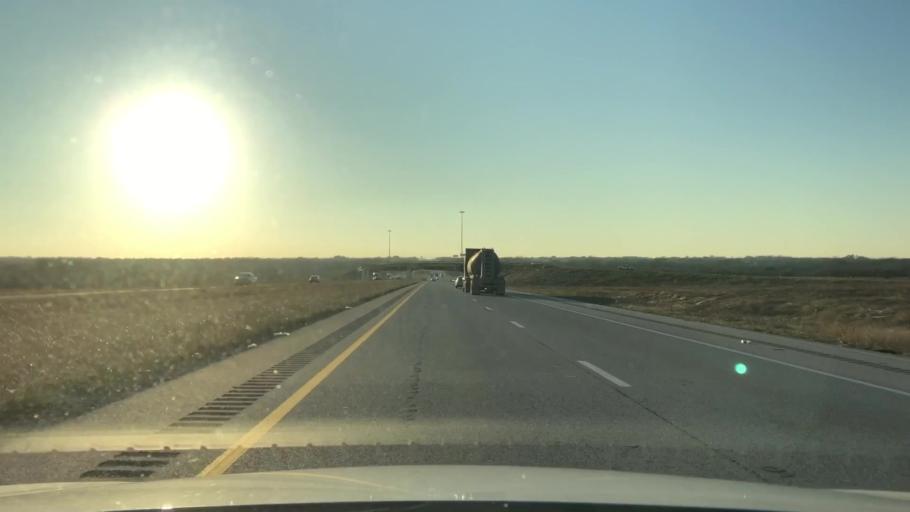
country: US
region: Texas
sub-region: Guadalupe County
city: Seguin
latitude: 29.6091
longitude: -97.8752
